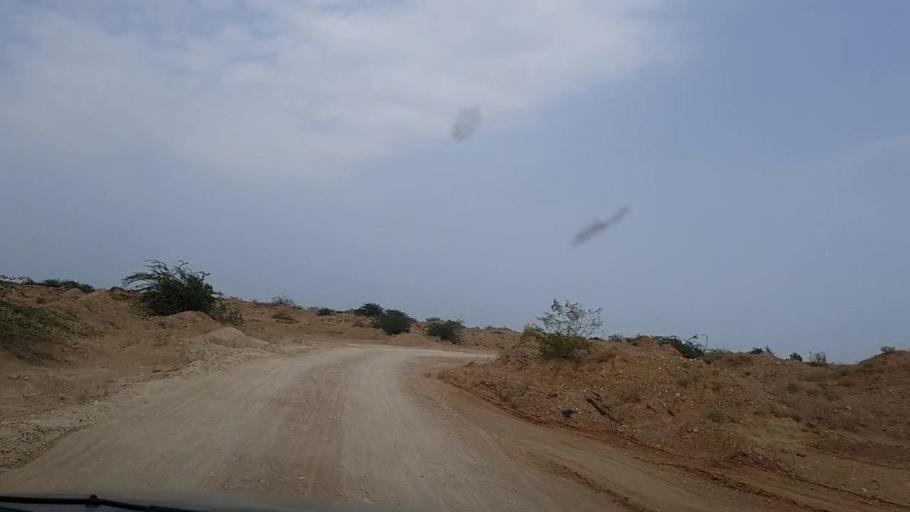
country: PK
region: Sindh
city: Kotri
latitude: 25.2823
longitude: 68.2643
